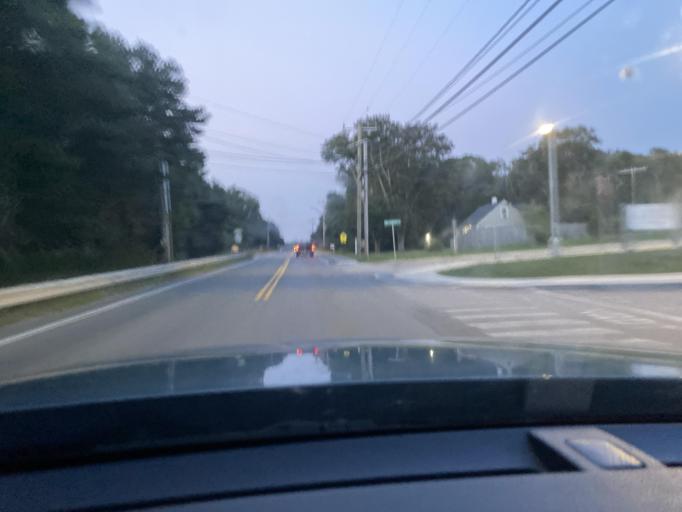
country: US
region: Massachusetts
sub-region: Barnstable County
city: Bourne
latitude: 41.7411
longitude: -70.5925
